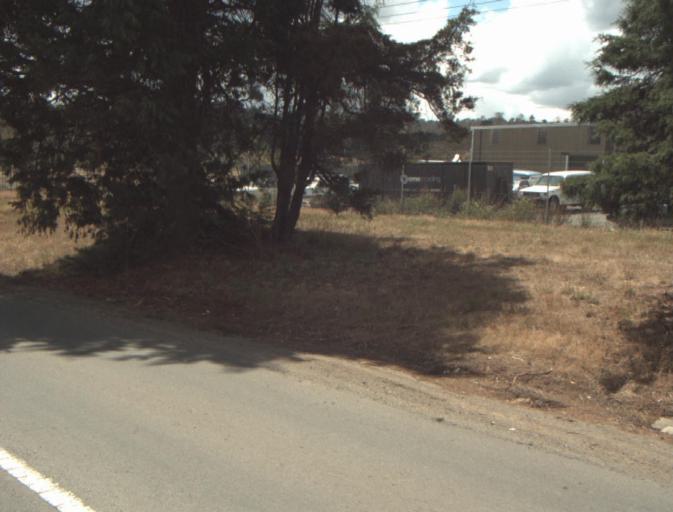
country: AU
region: Tasmania
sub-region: Launceston
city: Newnham
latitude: -41.4036
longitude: 147.1486
